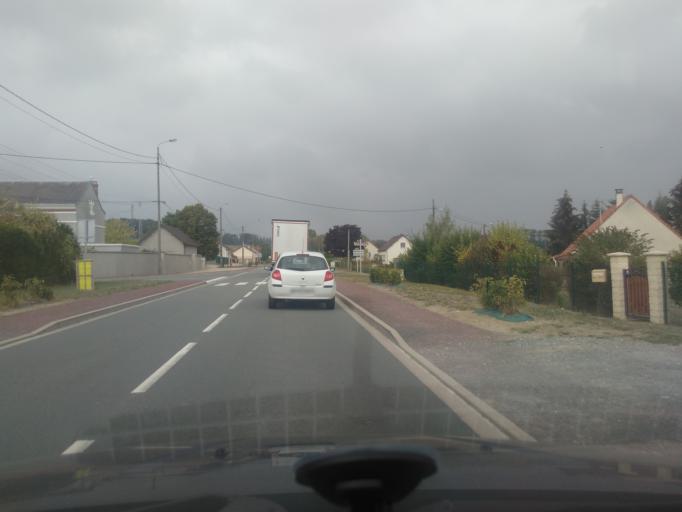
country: FR
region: Picardie
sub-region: Departement de l'Aisne
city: Saint-Erme-Outre-et-Ramecourt
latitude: 49.4657
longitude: 3.8201
